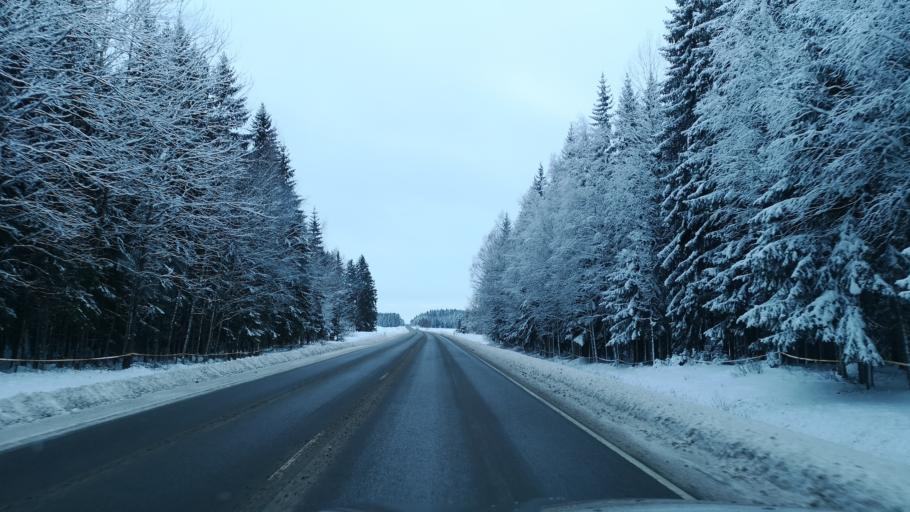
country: FI
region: Varsinais-Suomi
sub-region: Loimaa
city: Loimaa
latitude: 60.9095
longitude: 23.1658
